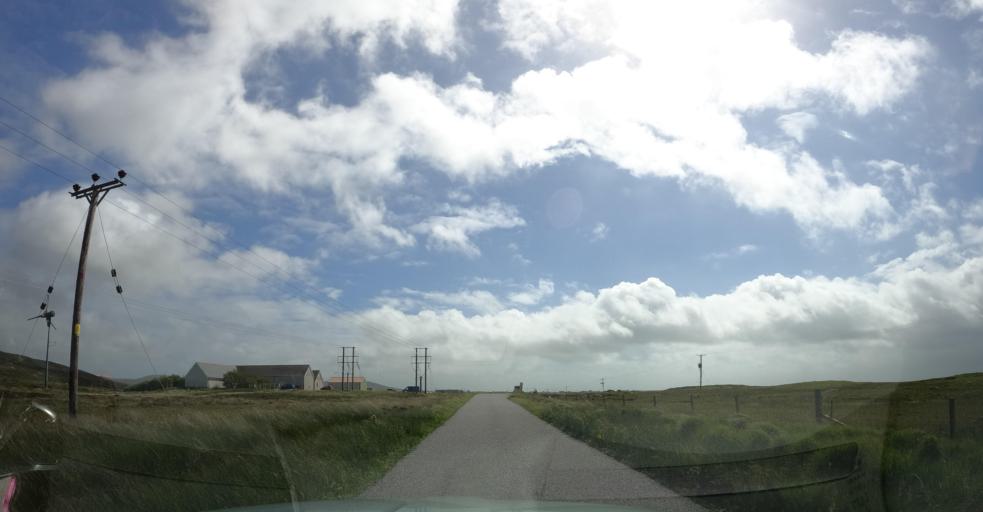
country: GB
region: Scotland
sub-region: Eilean Siar
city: Isle of South Uist
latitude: 57.2229
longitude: -7.3969
